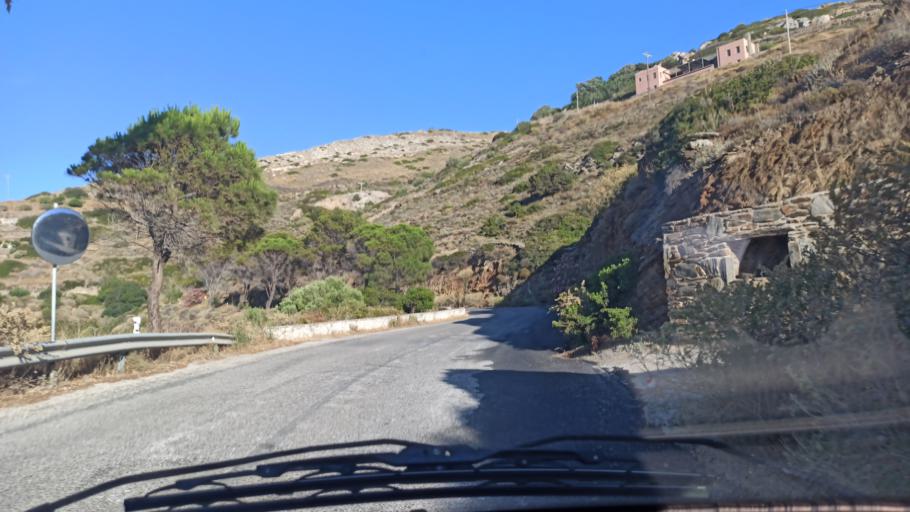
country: GR
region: South Aegean
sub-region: Nomos Kykladon
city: Ano Syros
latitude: 37.4424
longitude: 24.9096
